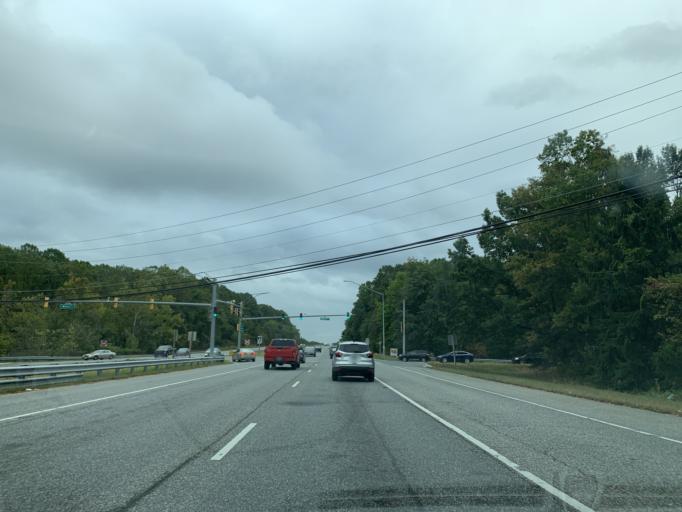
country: US
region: Maryland
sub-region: Harford County
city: Bel Air South
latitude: 39.4929
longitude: -76.3273
